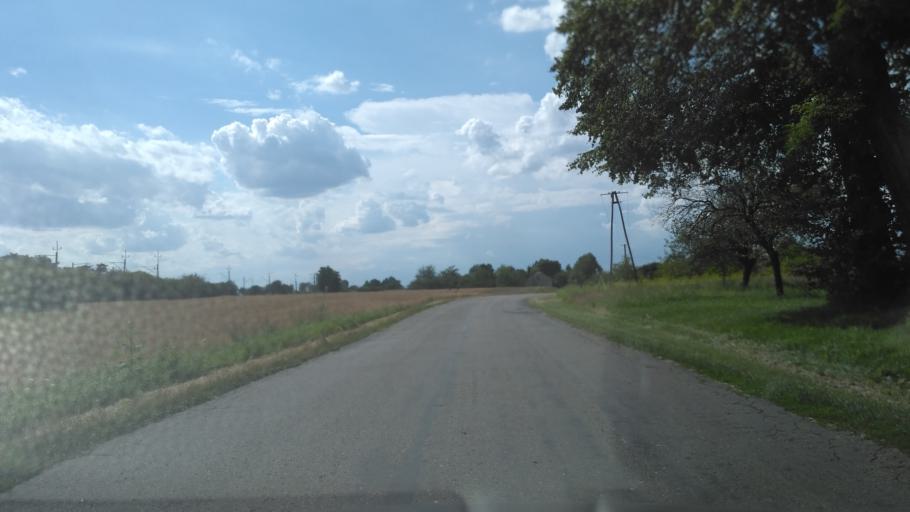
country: PL
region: Lublin Voivodeship
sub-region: Powiat leczynski
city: Milejow
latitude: 51.2102
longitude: 22.8766
